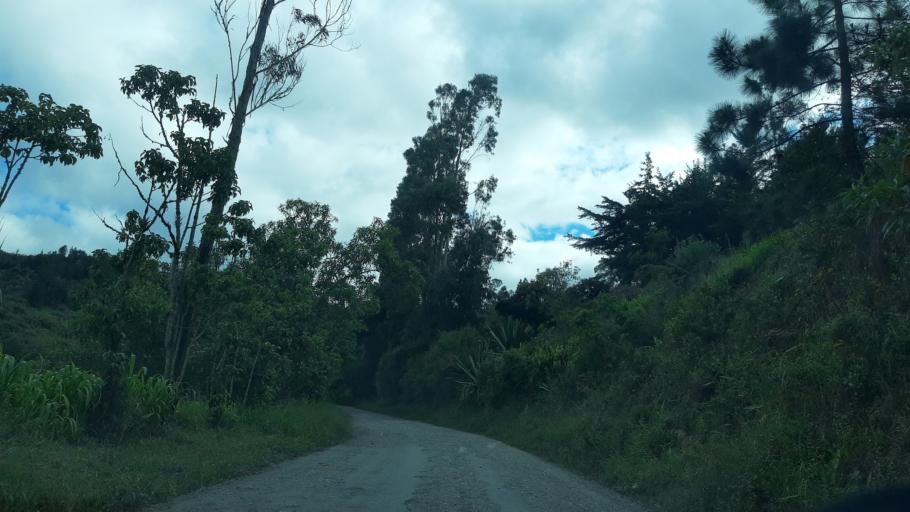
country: CO
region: Cundinamarca
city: Tenza
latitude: 5.0441
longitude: -73.4183
